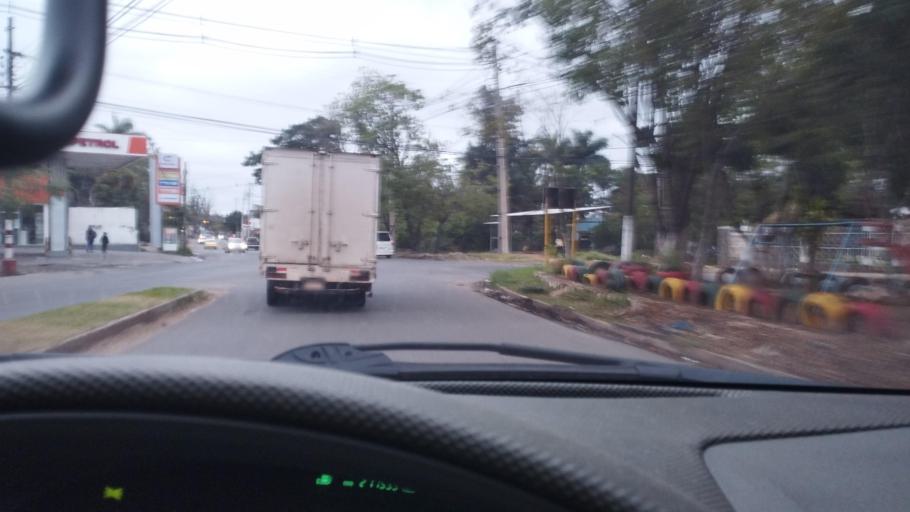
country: PY
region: Central
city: Fernando de la Mora
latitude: -25.2844
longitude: -57.5218
